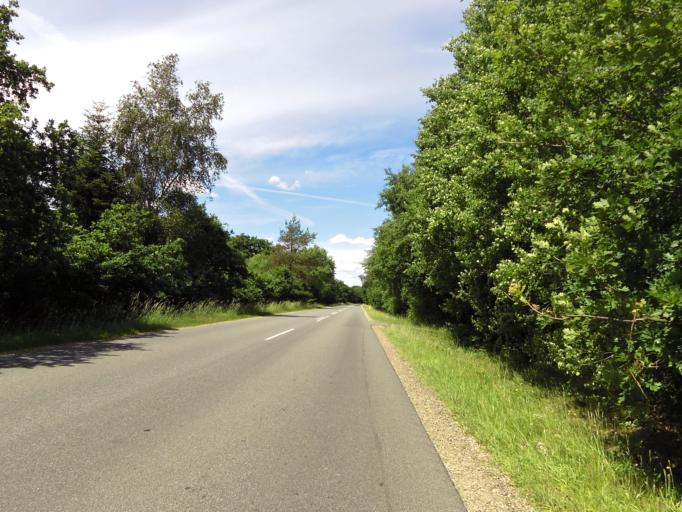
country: DK
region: South Denmark
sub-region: Esbjerg Kommune
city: Ribe
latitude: 55.2915
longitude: 8.7777
